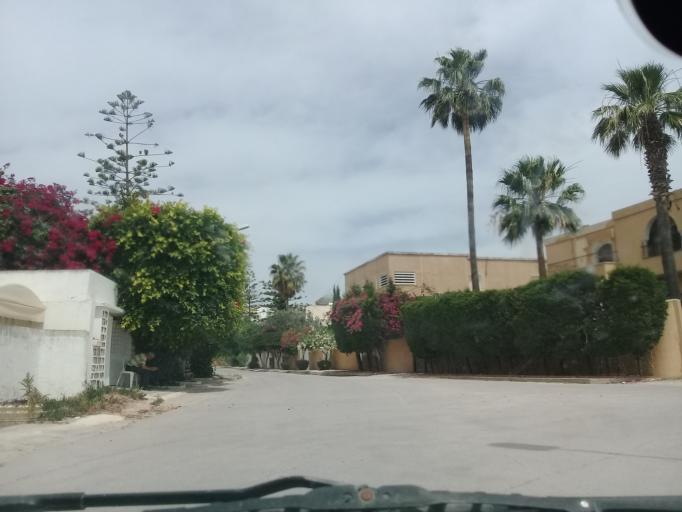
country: TN
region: Tunis
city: Tunis
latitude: 36.8408
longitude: 10.1587
